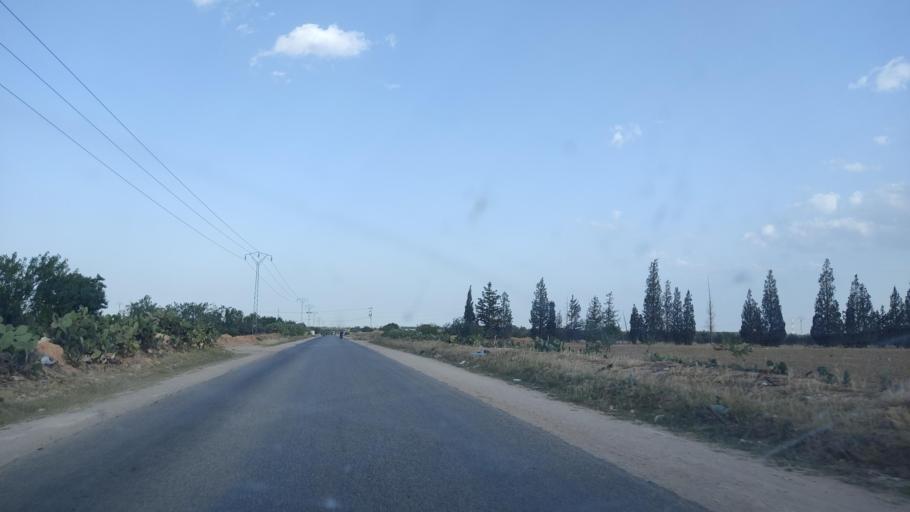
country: TN
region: Safaqis
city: Sfax
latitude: 34.8386
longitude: 10.6263
